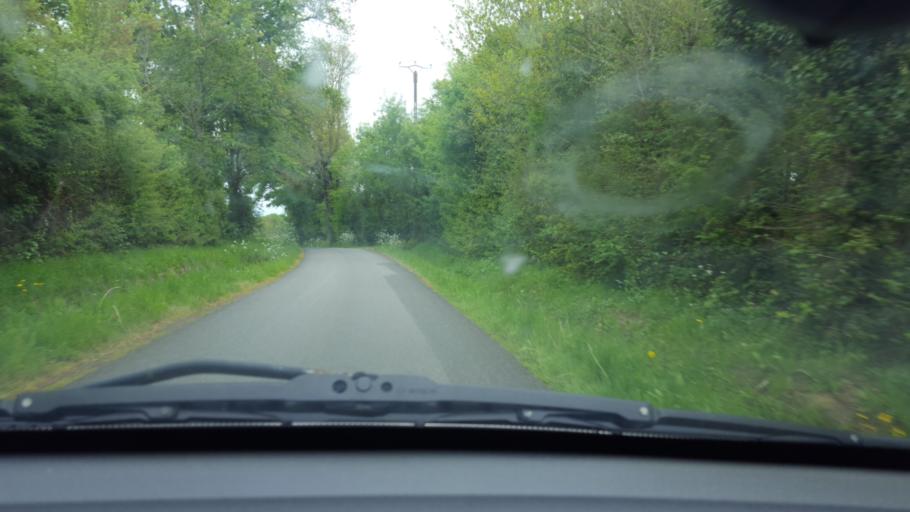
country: FR
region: Pays de la Loire
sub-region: Departement de la Loire-Atlantique
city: La Limouziniere
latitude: 47.0245
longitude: -1.5983
